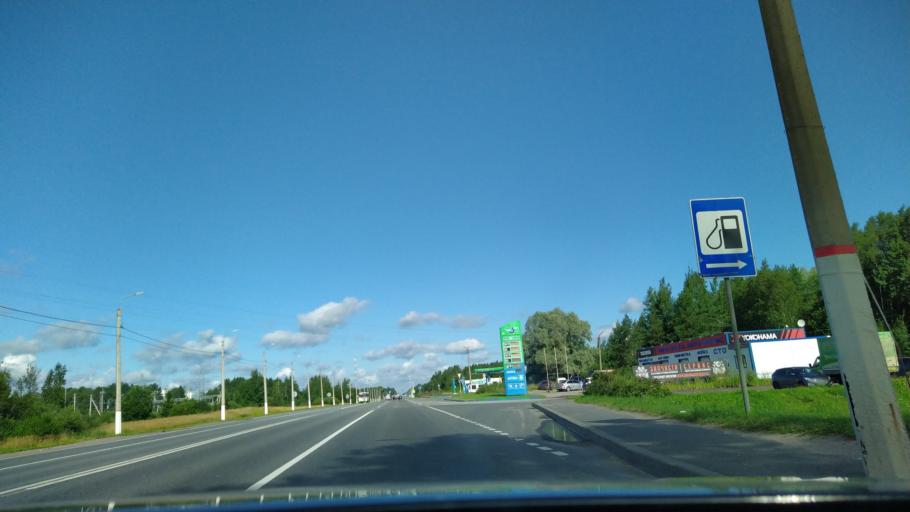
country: RU
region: Leningrad
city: Tosno
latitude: 59.5641
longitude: 30.8349
